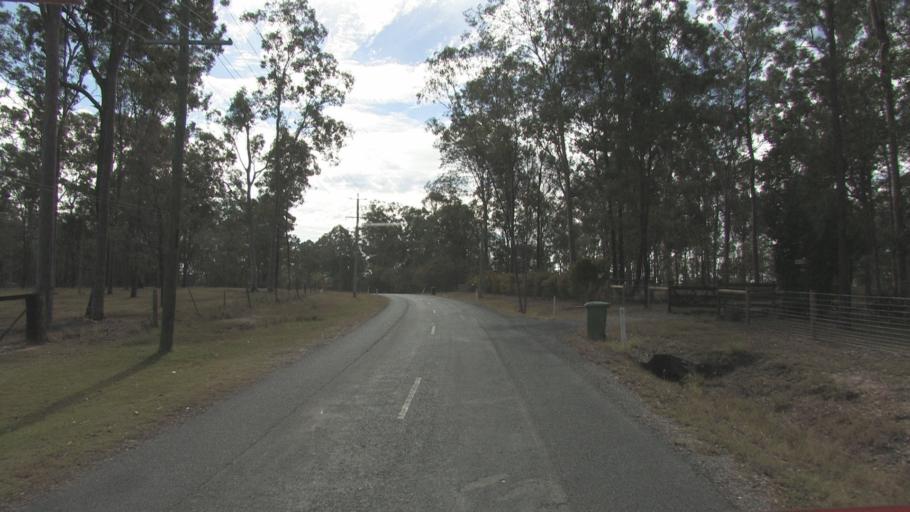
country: AU
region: Queensland
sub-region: Logan
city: North Maclean
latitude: -27.7557
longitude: 152.9746
